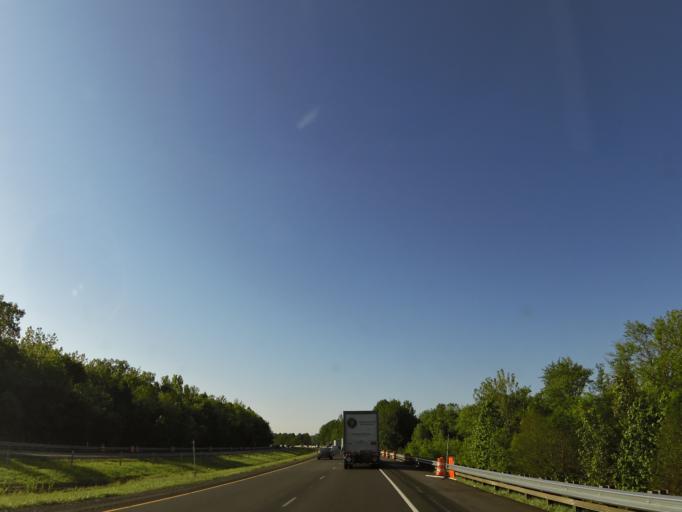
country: US
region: Indiana
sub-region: Jackson County
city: Seymour
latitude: 38.9177
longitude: -85.8352
